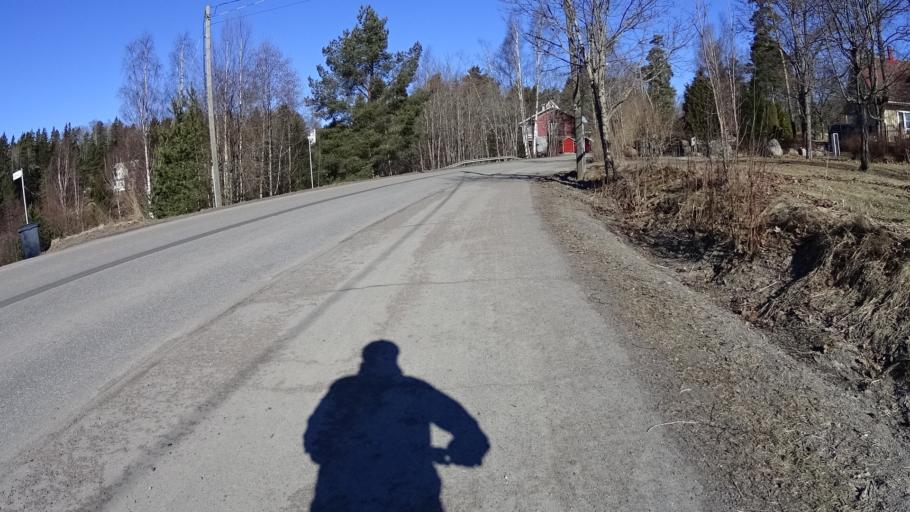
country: FI
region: Uusimaa
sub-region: Helsinki
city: Espoo
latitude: 60.2313
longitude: 24.6599
